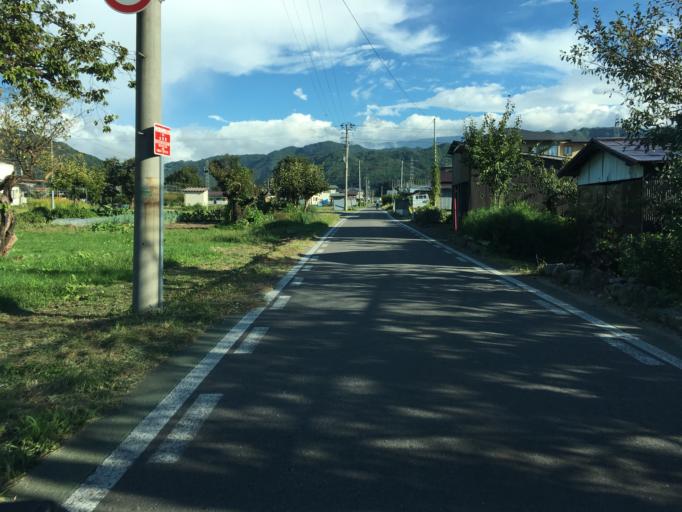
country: JP
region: Yamagata
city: Yonezawa
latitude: 37.8735
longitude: 140.1405
